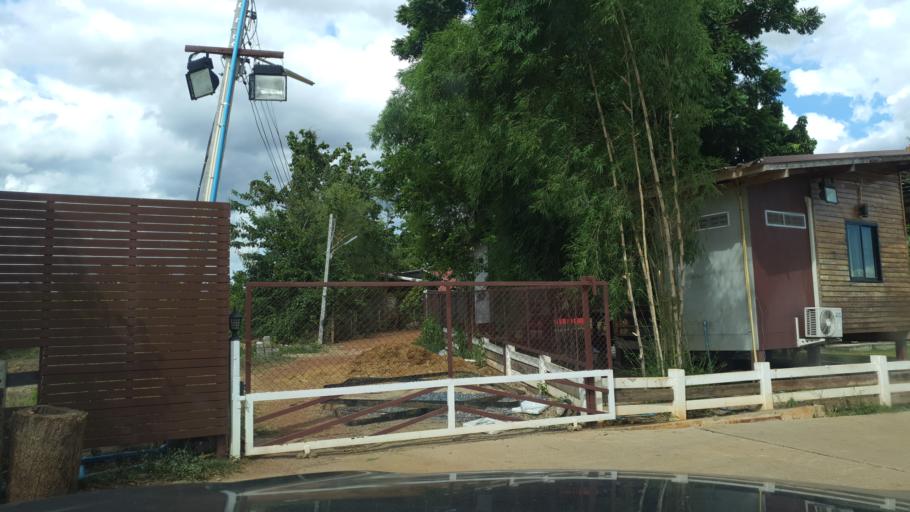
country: TH
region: Sukhothai
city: Thung Saliam
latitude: 17.3268
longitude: 99.5439
